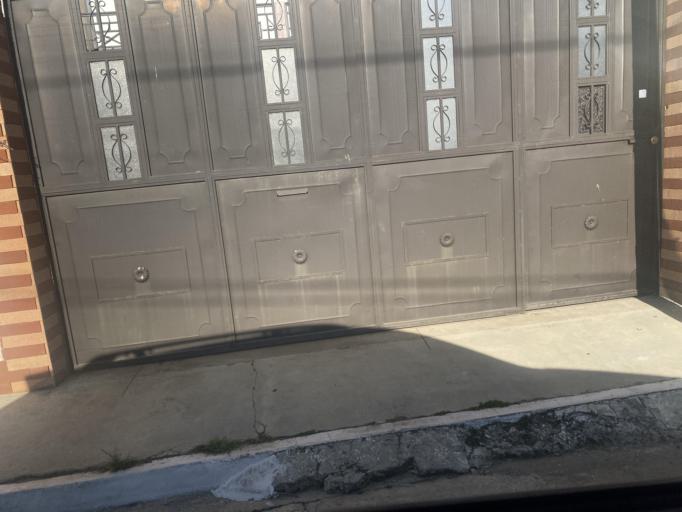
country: GT
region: Quetzaltenango
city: Olintepeque
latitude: 14.8704
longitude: -91.5175
